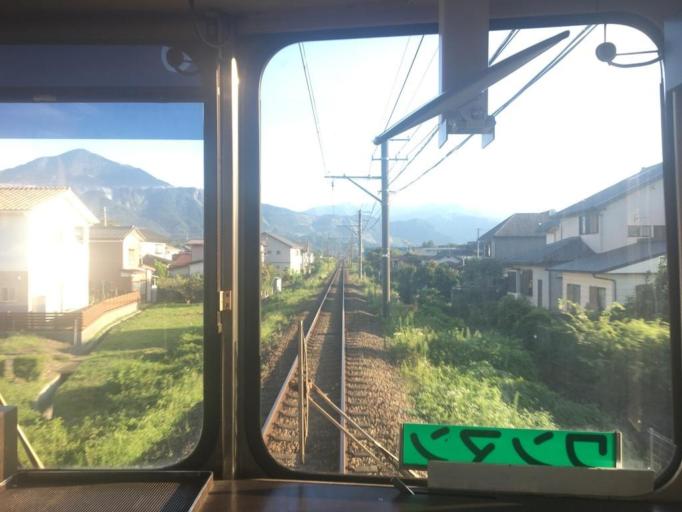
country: JP
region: Saitama
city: Chichibu
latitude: 36.0058
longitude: 139.0885
